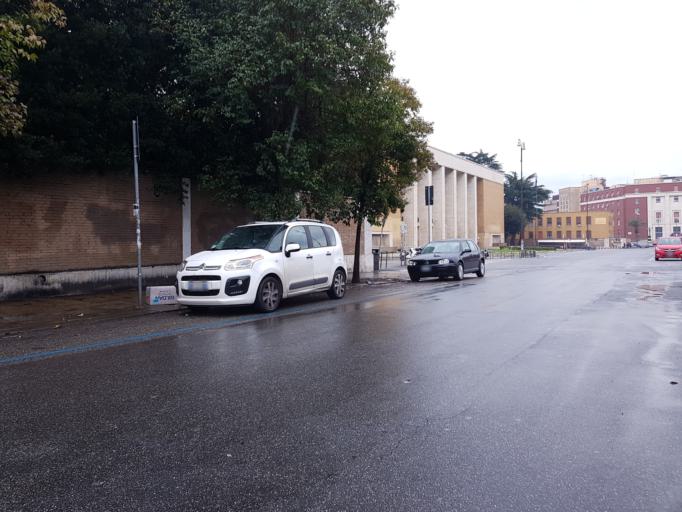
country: IT
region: Latium
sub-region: Citta metropolitana di Roma Capitale
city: Rome
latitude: 41.9031
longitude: 12.5114
